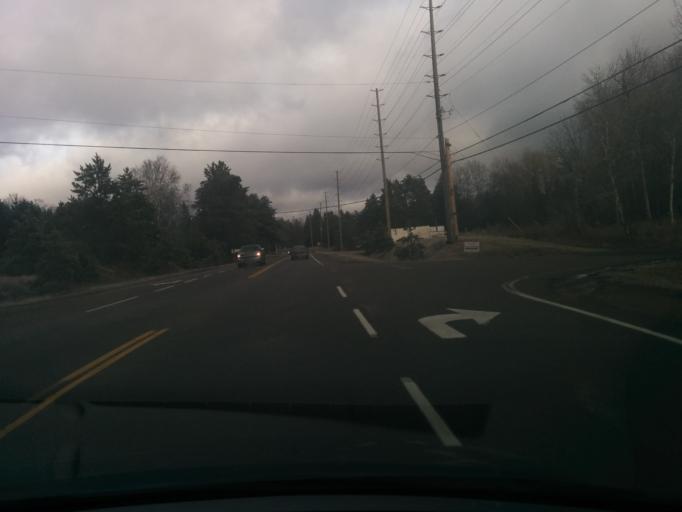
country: CA
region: Ontario
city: Bancroft
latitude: 45.0211
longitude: -78.5702
